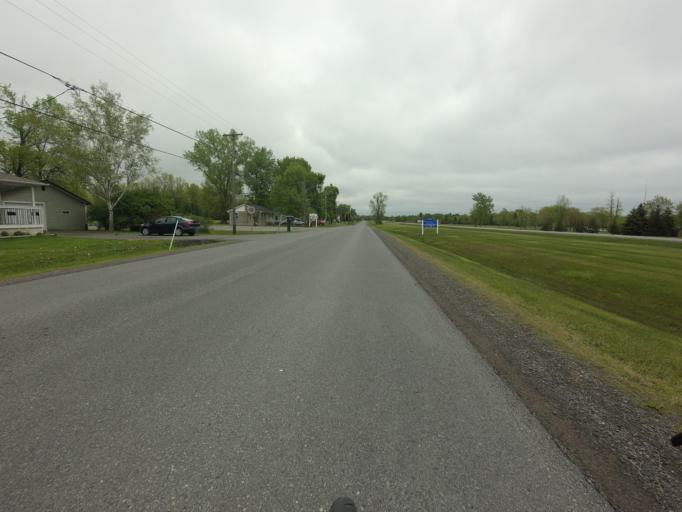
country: US
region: New York
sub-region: St. Lawrence County
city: Norfolk
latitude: 44.9340
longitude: -75.1258
